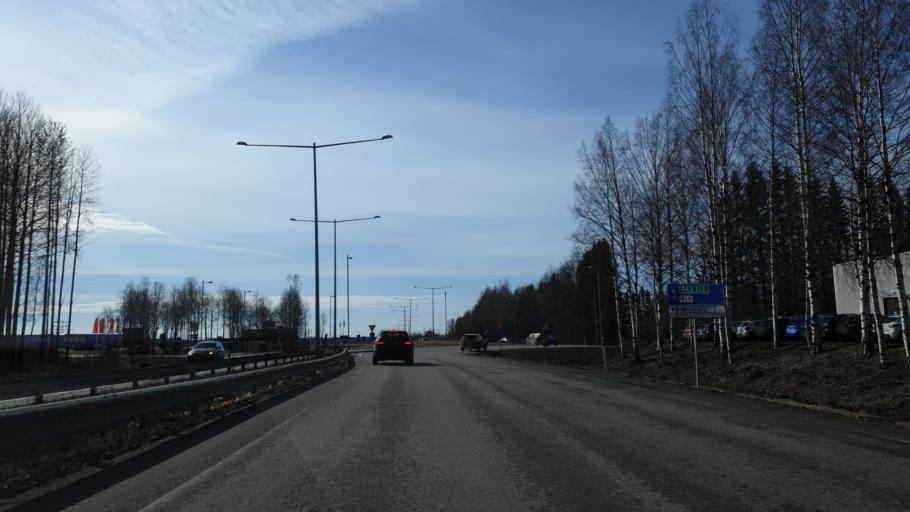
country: SE
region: Vaesterbotten
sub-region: Umea Kommun
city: Umea
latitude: 63.8128
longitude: 20.2493
